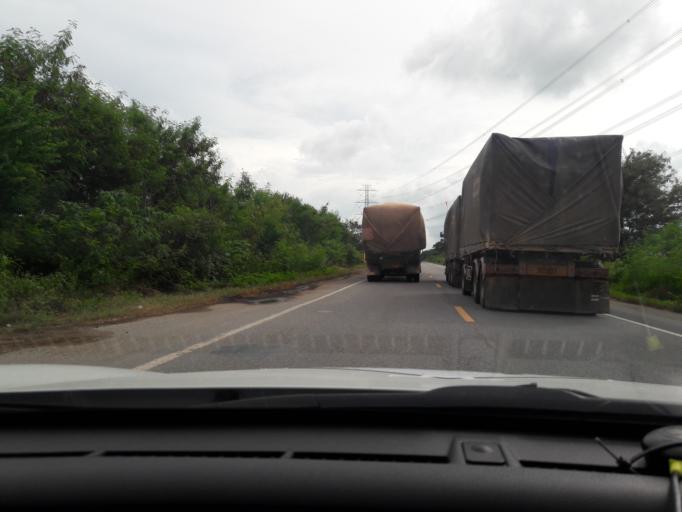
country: TH
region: Nakhon Sawan
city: Tak Fa
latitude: 15.4113
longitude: 100.5141
